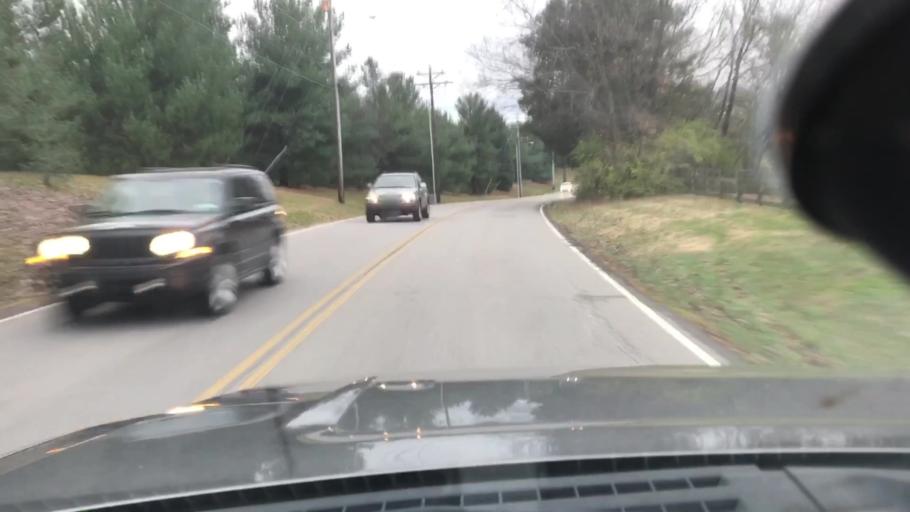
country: US
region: Tennessee
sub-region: Williamson County
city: Brentwood Estates
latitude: 35.9793
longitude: -86.7489
